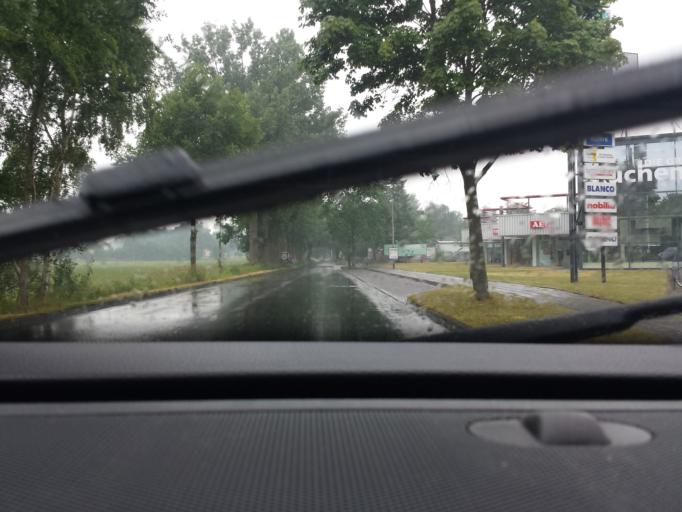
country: DE
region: North Rhine-Westphalia
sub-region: Regierungsbezirk Munster
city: Gronau
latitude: 52.2025
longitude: 7.0602
